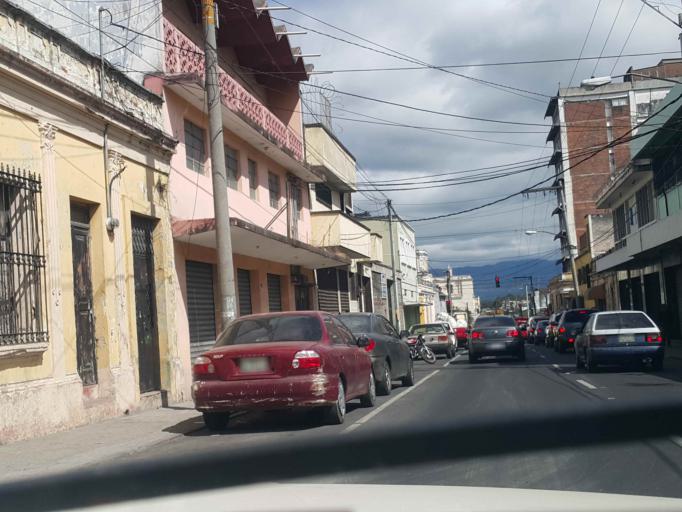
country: GT
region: Guatemala
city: Guatemala City
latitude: 14.6428
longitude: -90.5102
